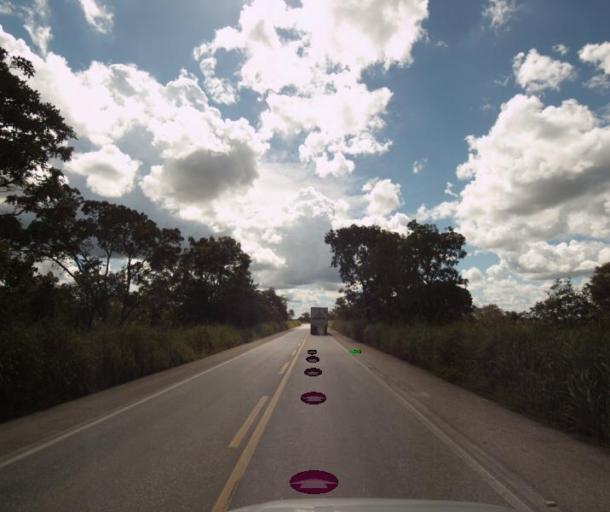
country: BR
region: Goias
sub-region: Porangatu
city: Porangatu
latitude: -13.5595
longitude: -49.0599
